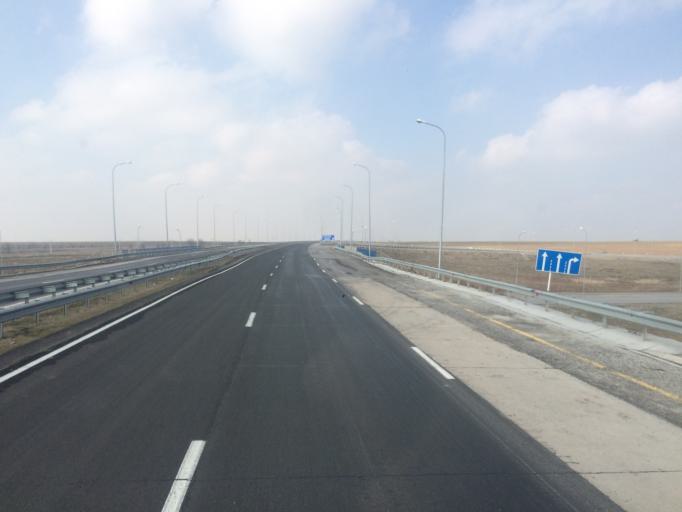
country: KZ
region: Ongtustik Qazaqstan
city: Temirlanovka
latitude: 42.5279
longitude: 69.3469
